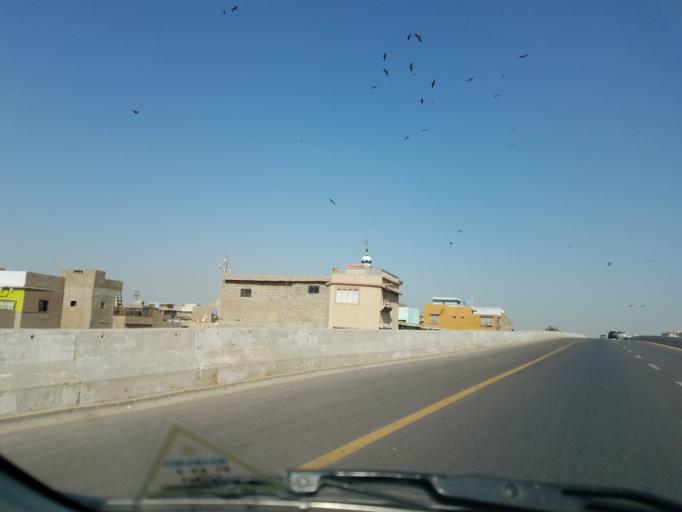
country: PK
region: Sindh
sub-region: Karachi District
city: Karachi
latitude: 24.8904
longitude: 67.0291
